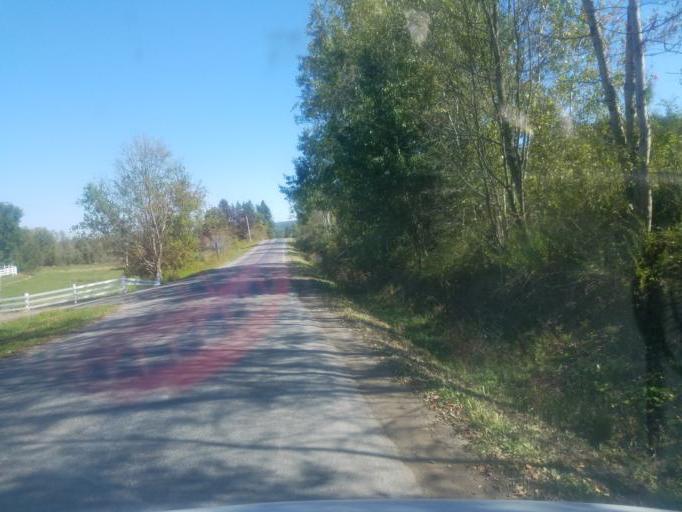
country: US
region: New York
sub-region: Allegany County
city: Friendship
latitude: 42.3015
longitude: -78.1982
